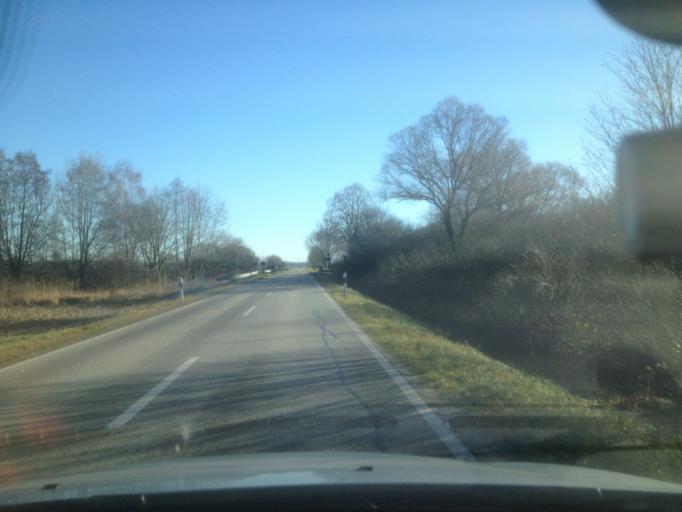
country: DE
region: Bavaria
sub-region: Upper Bavaria
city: Berglern
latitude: 48.4098
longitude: 11.9139
